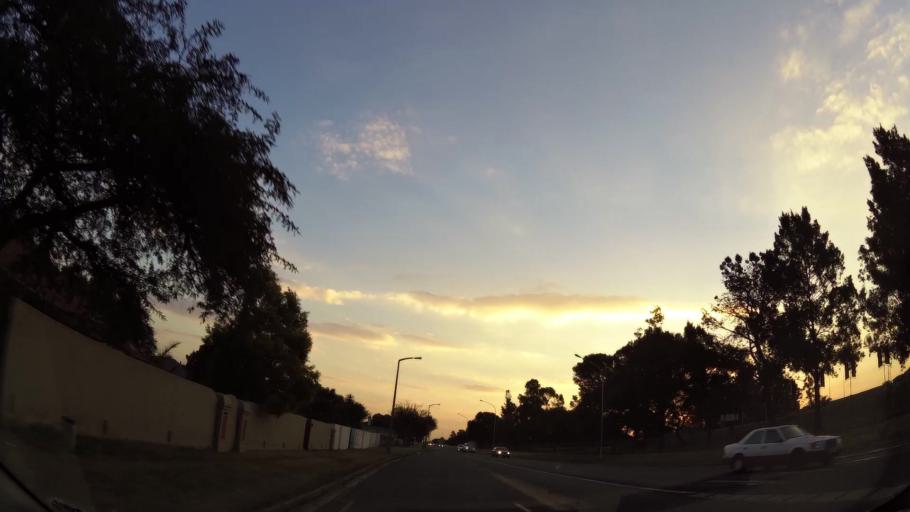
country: ZA
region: Gauteng
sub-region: Ekurhuleni Metropolitan Municipality
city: Benoni
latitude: -26.1765
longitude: 28.3183
